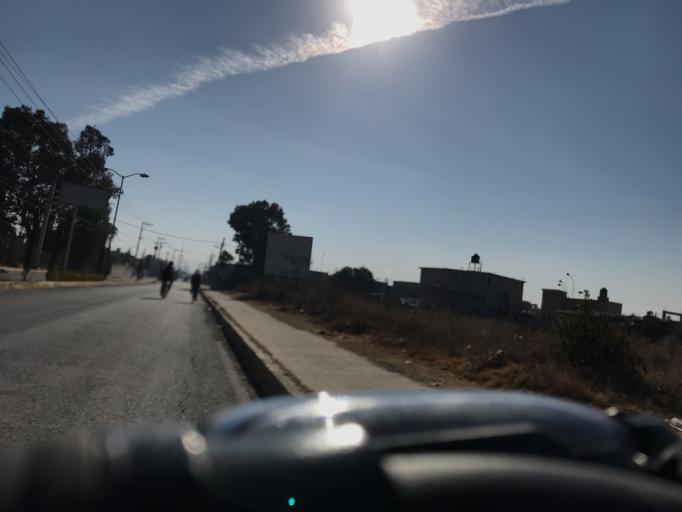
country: MX
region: Mexico
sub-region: Tonanitla
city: Colonia la Asuncion
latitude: 19.6930
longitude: -99.0647
